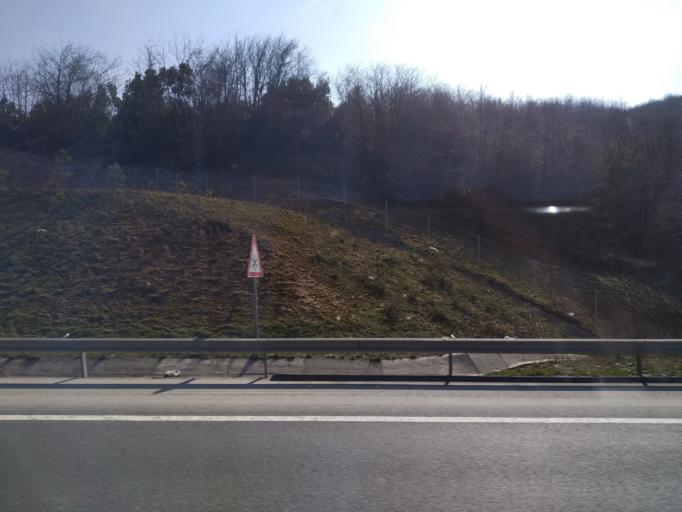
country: TR
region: Istanbul
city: Arikoey
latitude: 41.2316
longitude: 28.9476
